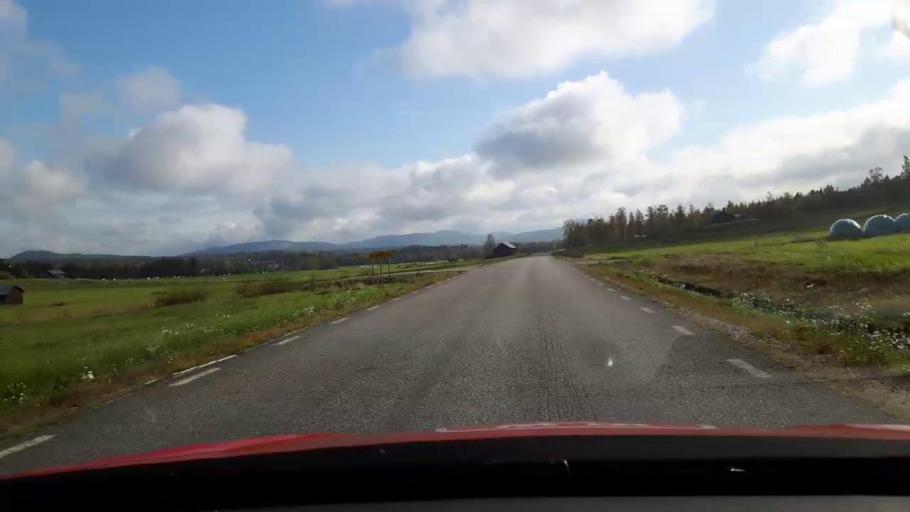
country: SE
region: Gaevleborg
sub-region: Ljusdals Kommun
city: Ljusdal
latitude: 61.7626
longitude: 16.0731
